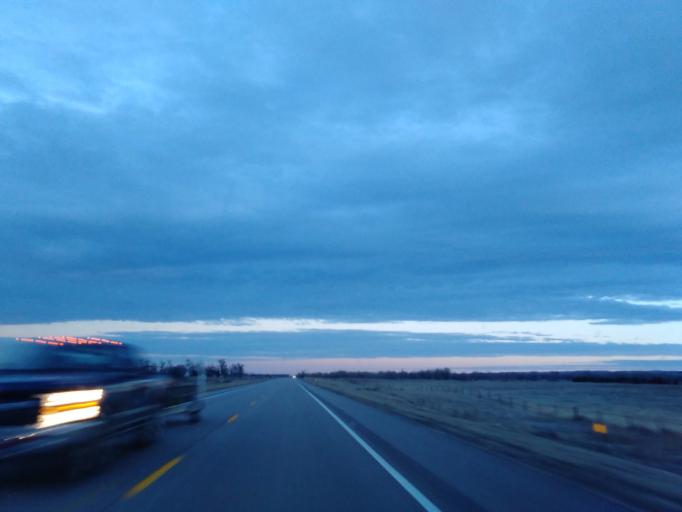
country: US
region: Nebraska
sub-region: Garden County
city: Oshkosh
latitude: 41.3687
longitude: -102.2393
